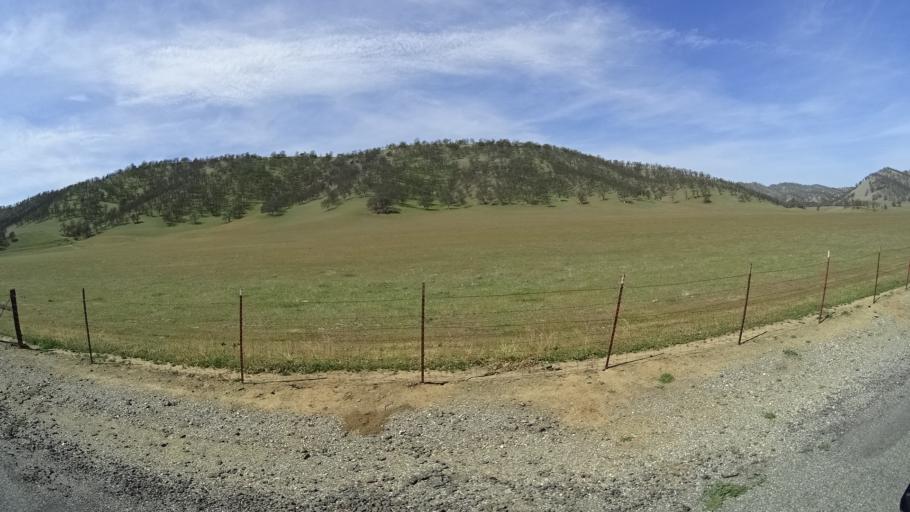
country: US
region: California
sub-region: Glenn County
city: Willows
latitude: 39.5238
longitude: -122.4567
